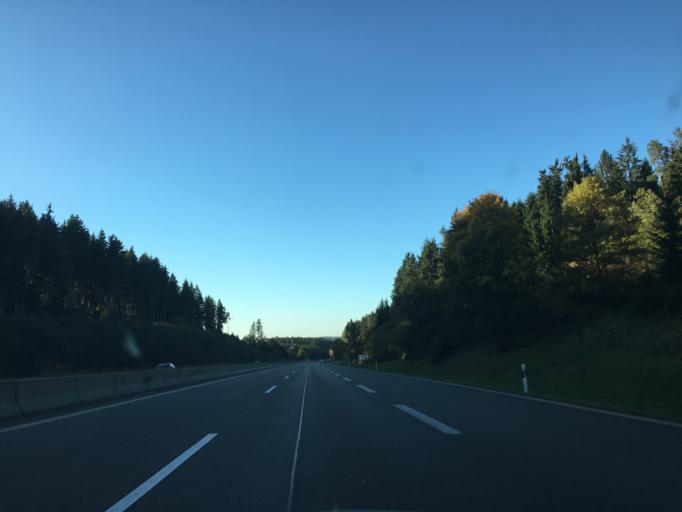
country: DE
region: Baden-Wuerttemberg
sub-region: Freiburg Region
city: Trossingen
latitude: 48.0678
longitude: 8.6099
